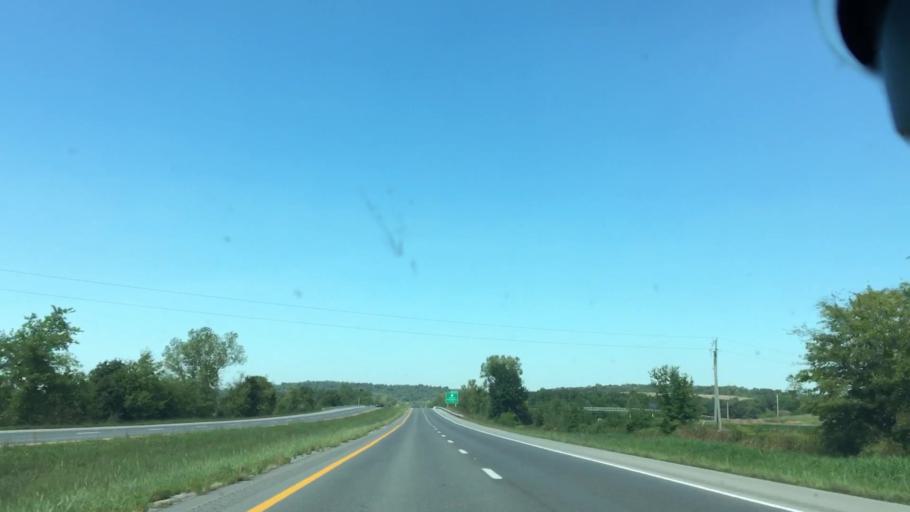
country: US
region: Kentucky
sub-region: Webster County
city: Sebree
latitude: 37.5776
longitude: -87.4822
